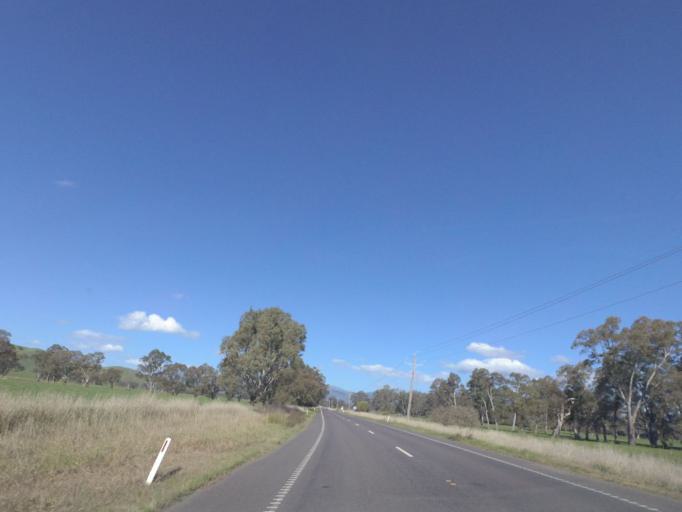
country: AU
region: Victoria
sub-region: Murrindindi
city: Alexandra
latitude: -37.2207
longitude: 145.7355
